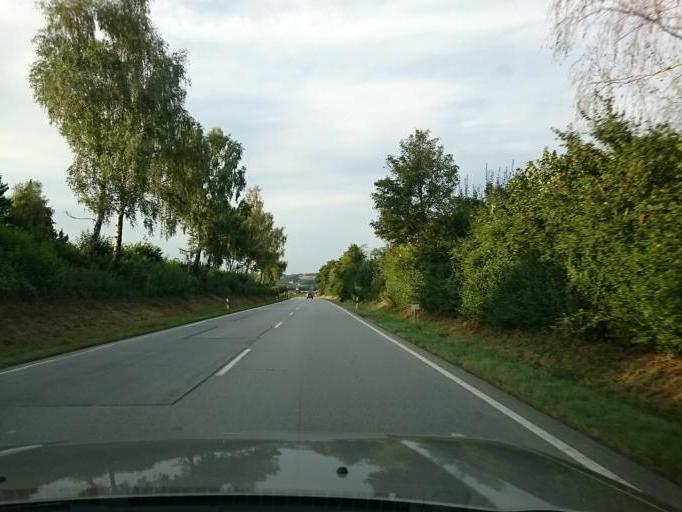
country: DE
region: Bavaria
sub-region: Lower Bavaria
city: Simbach
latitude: 48.5937
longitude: 12.7187
